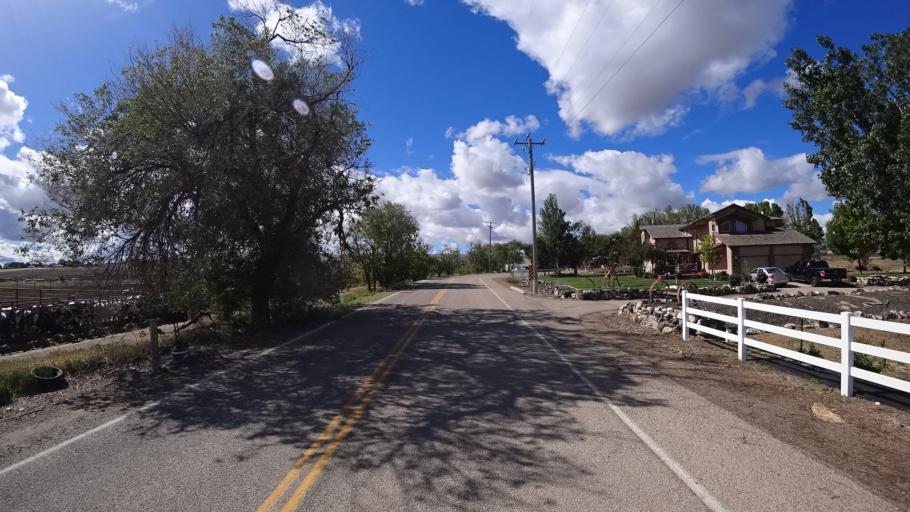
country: US
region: Idaho
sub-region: Ada County
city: Kuna
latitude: 43.4654
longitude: -116.4636
